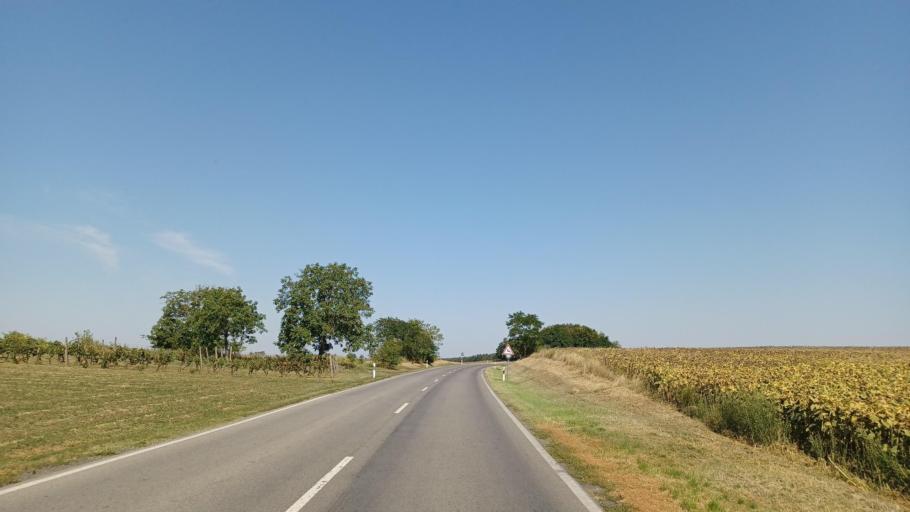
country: HU
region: Tolna
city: Nagydorog
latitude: 46.6443
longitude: 18.6492
